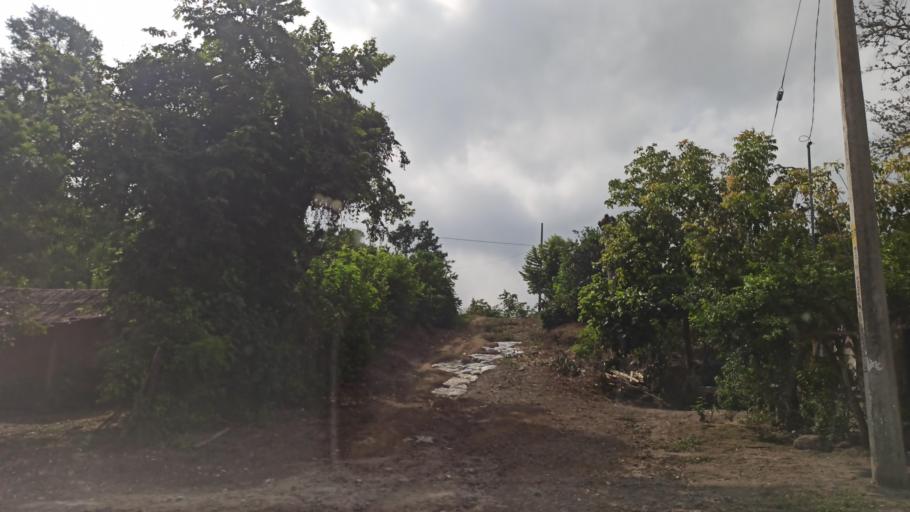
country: MX
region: Puebla
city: San Jose Acateno
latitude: 20.1605
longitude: -97.1836
